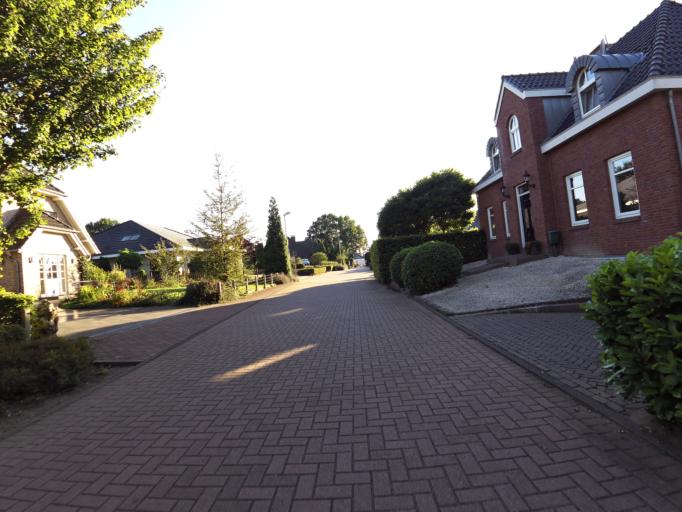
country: DE
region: North Rhine-Westphalia
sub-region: Regierungsbezirk Dusseldorf
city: Emmerich
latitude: 51.8709
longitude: 6.1671
